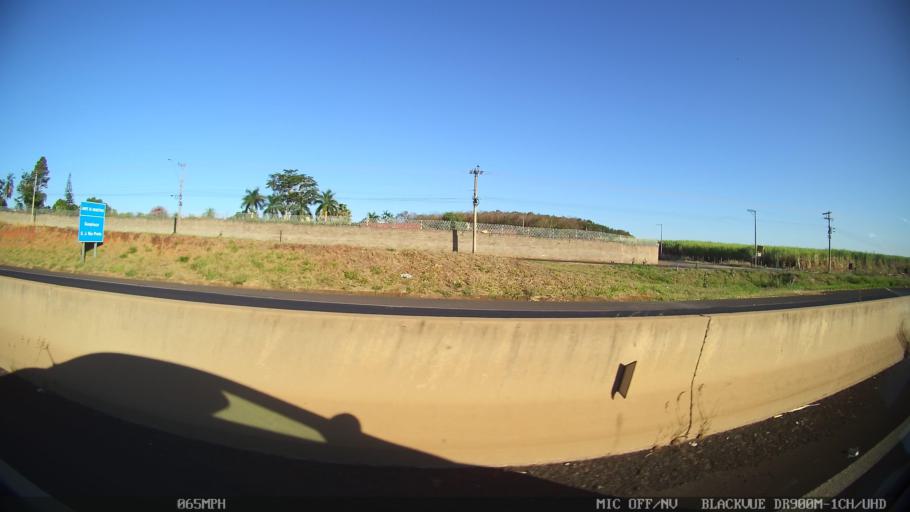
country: BR
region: Sao Paulo
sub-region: Guapiacu
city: Guapiacu
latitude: -20.7867
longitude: -49.2803
